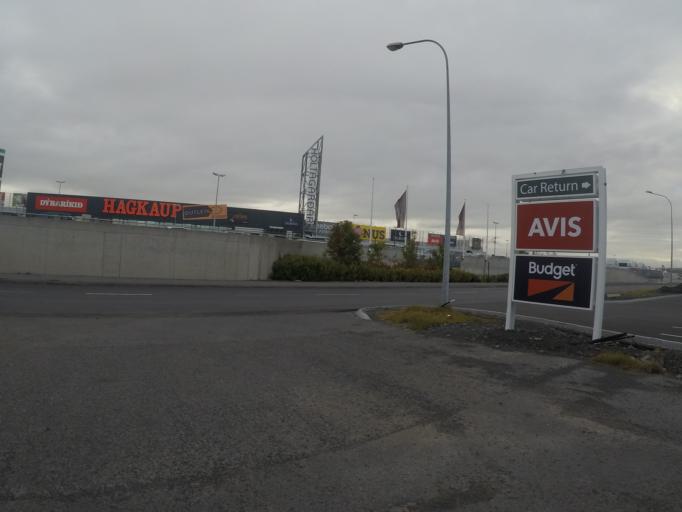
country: IS
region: Capital Region
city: Reykjavik
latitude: 64.1422
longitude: -21.8498
